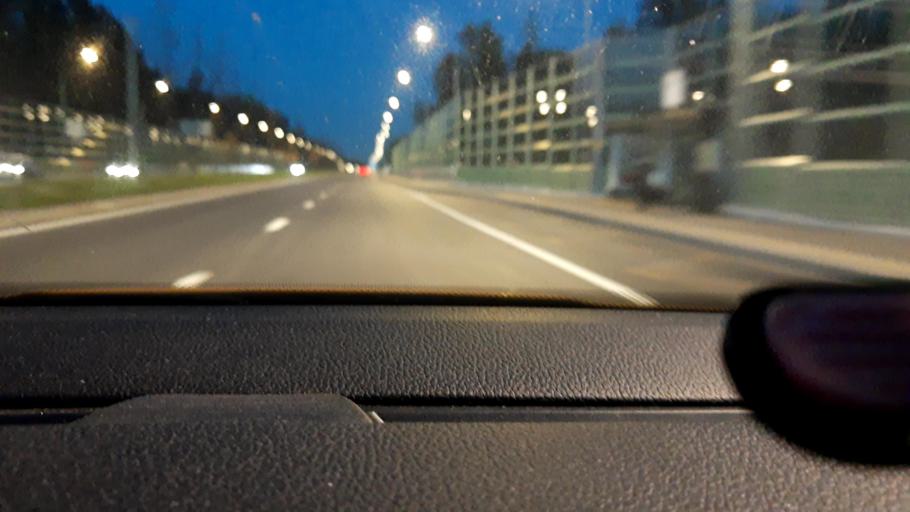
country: RU
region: Moskovskaya
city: Filimonki
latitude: 55.5713
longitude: 37.3595
